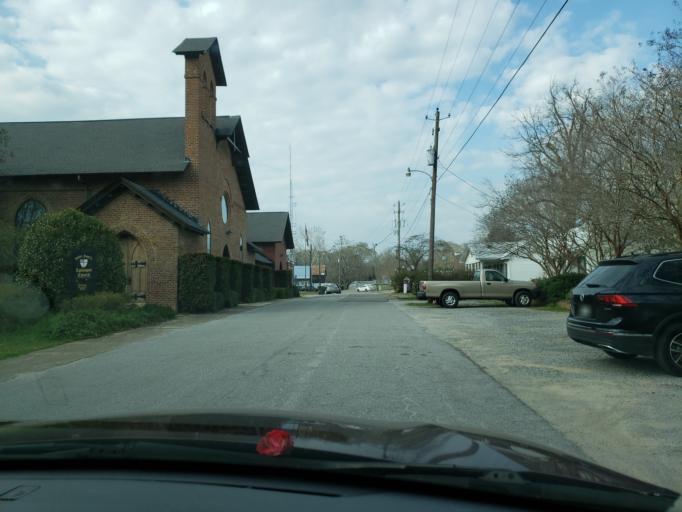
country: US
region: Alabama
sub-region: Hale County
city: Greensboro
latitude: 32.7032
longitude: -87.5965
